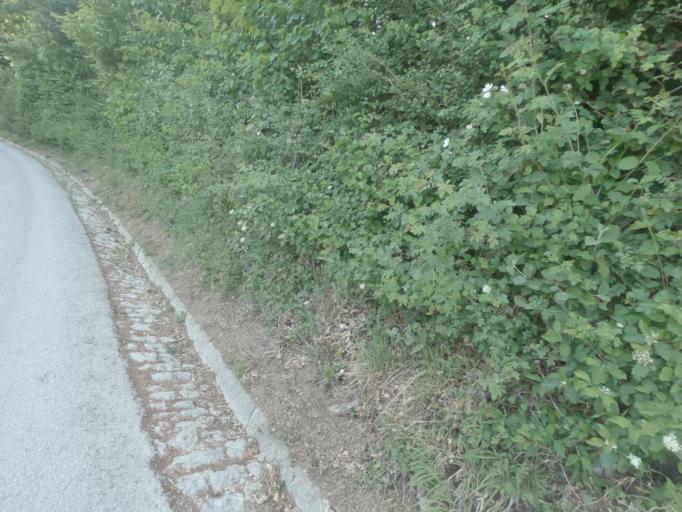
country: CH
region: Solothurn
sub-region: Bezirk Lebern
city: Langendorf
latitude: 47.2363
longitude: 7.4948
